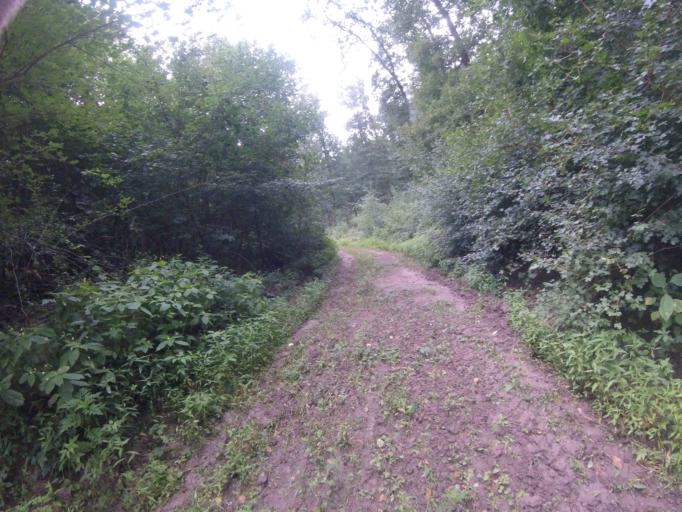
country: SK
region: Nitriansky
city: Sahy
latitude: 48.0507
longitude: 18.9709
